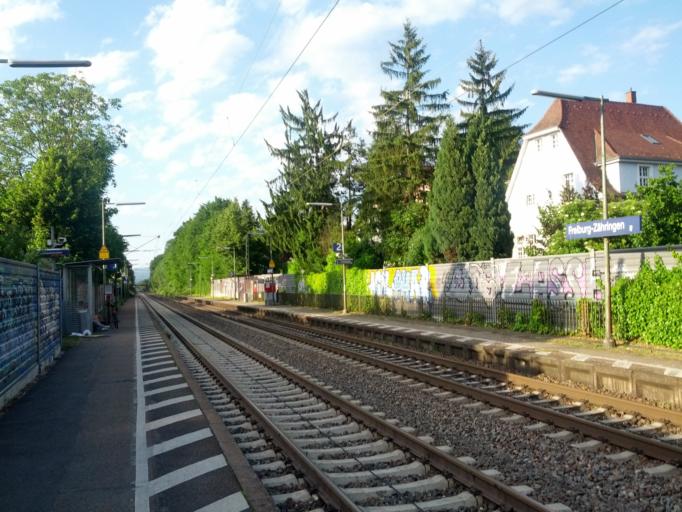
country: DE
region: Baden-Wuerttemberg
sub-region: Freiburg Region
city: Gundelfingen
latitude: 48.0242
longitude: 7.8636
